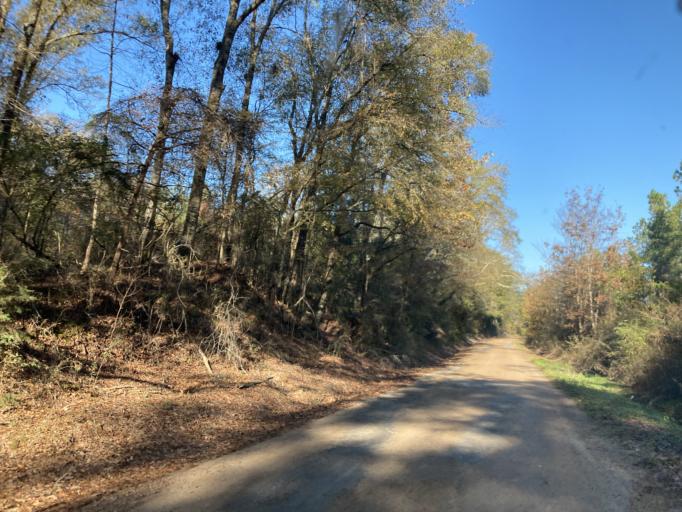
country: US
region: Mississippi
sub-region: Madison County
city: Kearney Park
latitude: 32.7348
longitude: -90.1978
